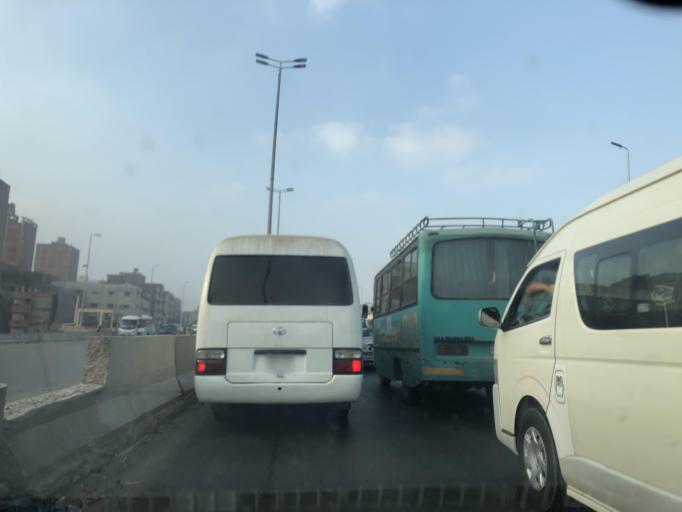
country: EG
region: Al Jizah
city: Awsim
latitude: 30.0731
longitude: 31.1759
